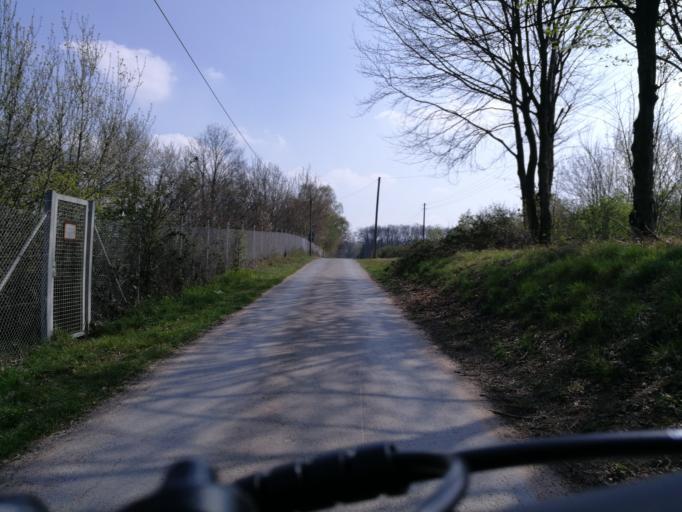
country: DE
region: North Rhine-Westphalia
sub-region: Regierungsbezirk Dusseldorf
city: Dormagen
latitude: 51.1446
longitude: 6.7793
